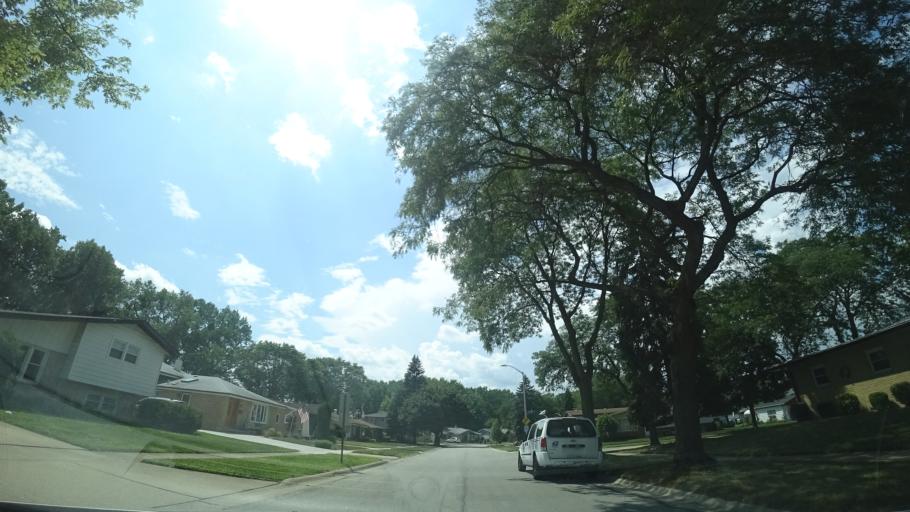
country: US
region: Illinois
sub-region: Cook County
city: Alsip
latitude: 41.6771
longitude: -87.7319
